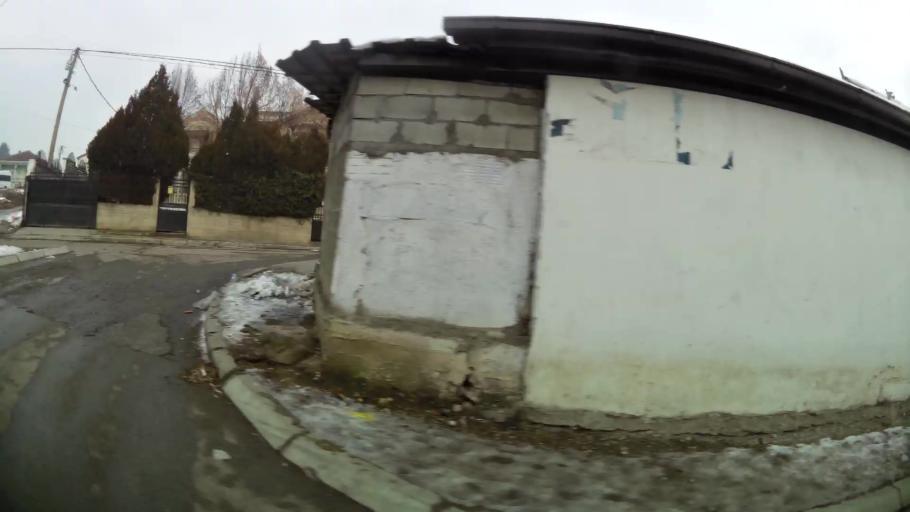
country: MK
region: Suto Orizari
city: Suto Orizare
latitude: 42.0381
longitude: 21.4270
